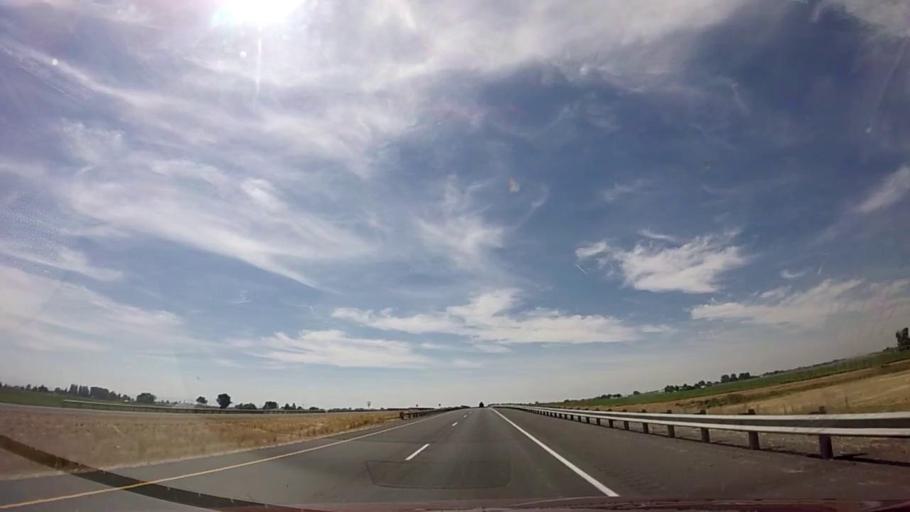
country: US
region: Idaho
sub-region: Minidoka County
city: Rupert
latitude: 42.5691
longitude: -113.6594
